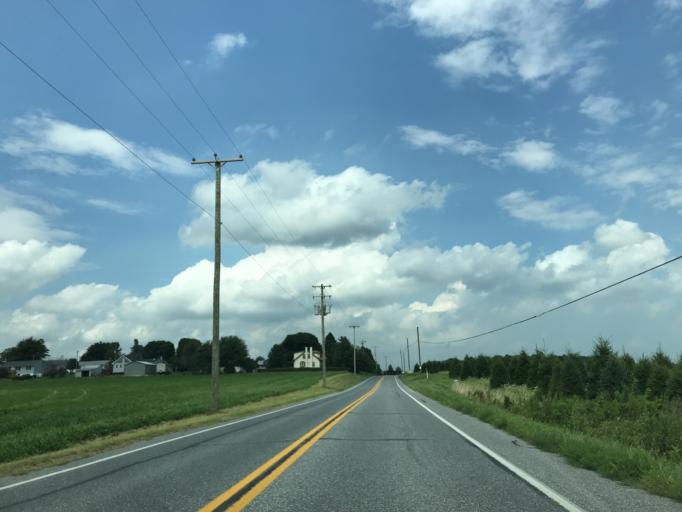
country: US
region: Pennsylvania
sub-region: York County
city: Red Lion
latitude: 39.8569
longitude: -76.6212
